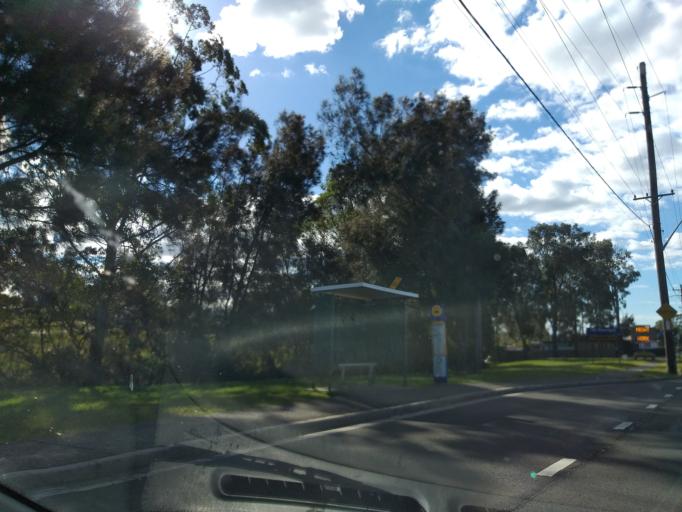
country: AU
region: New South Wales
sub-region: Shellharbour
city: Barrack Heights
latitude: -34.5596
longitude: 150.8431
